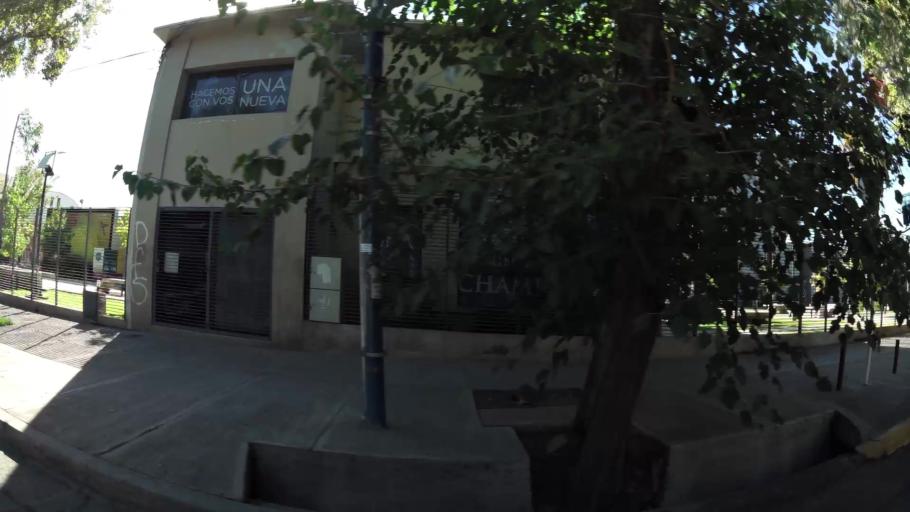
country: AR
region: Mendoza
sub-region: Departamento de Godoy Cruz
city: Godoy Cruz
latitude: -32.9165
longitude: -68.8427
